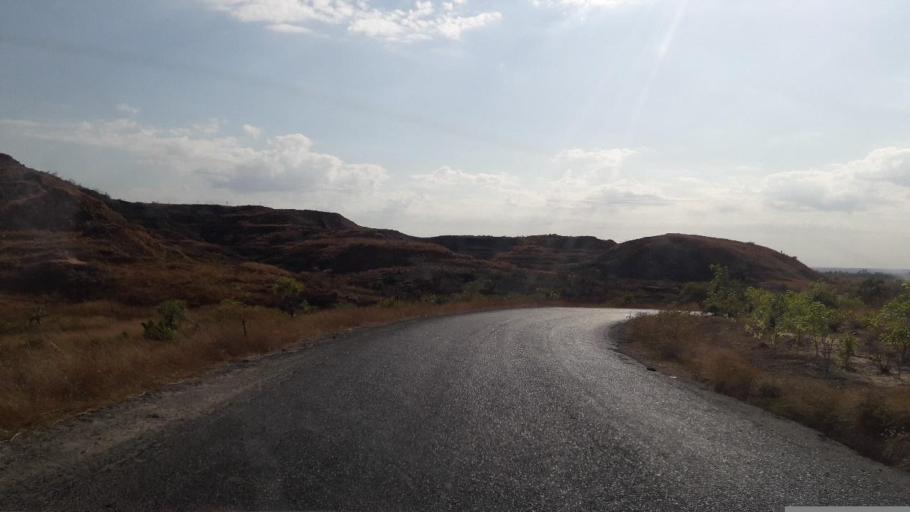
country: MG
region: Boeny
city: Marovoay
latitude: -15.9020
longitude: 46.6111
